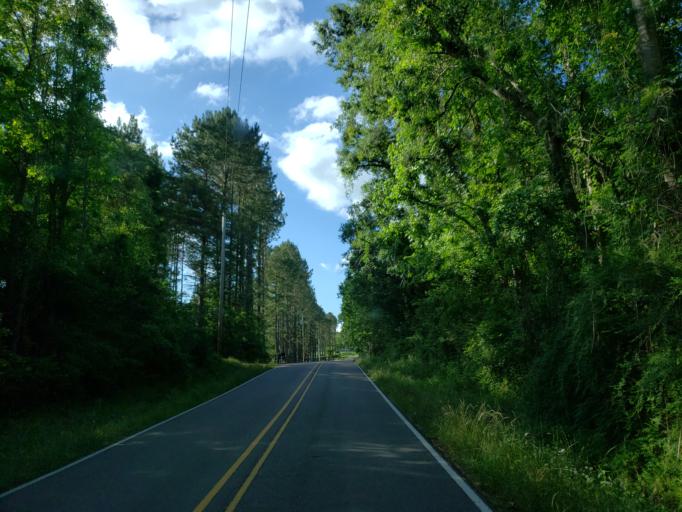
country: US
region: Mississippi
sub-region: Forrest County
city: Petal
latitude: 31.3210
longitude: -89.2111
